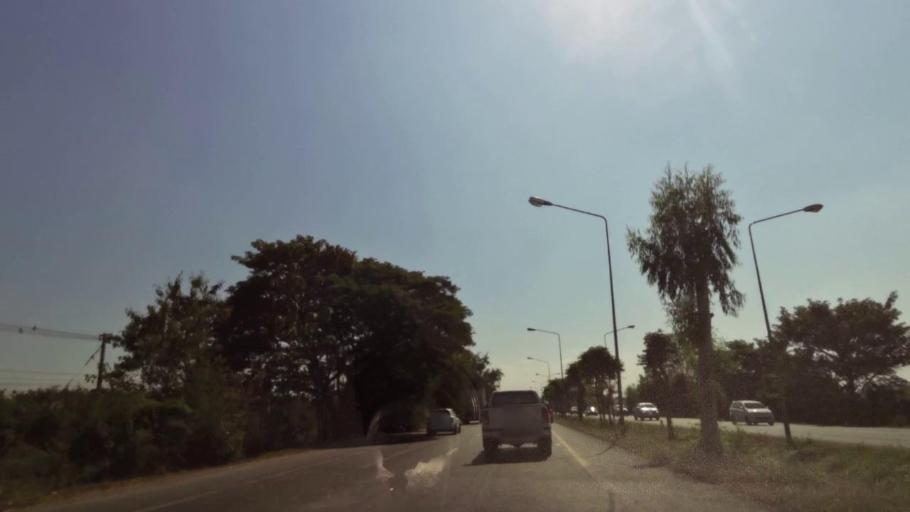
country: TH
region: Nakhon Sawan
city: Kao Liao
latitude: 15.8002
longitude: 100.1204
